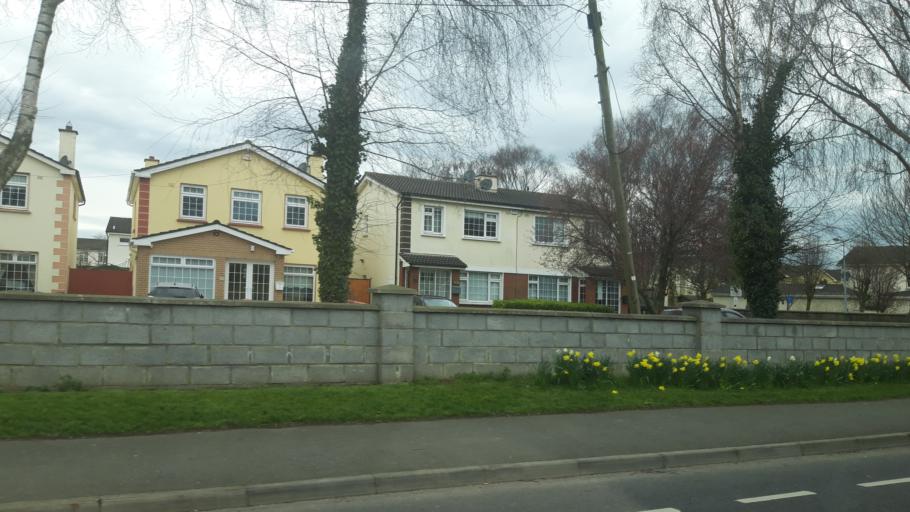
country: IE
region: Leinster
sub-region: Kildare
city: Celbridge
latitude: 53.3475
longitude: -6.5420
